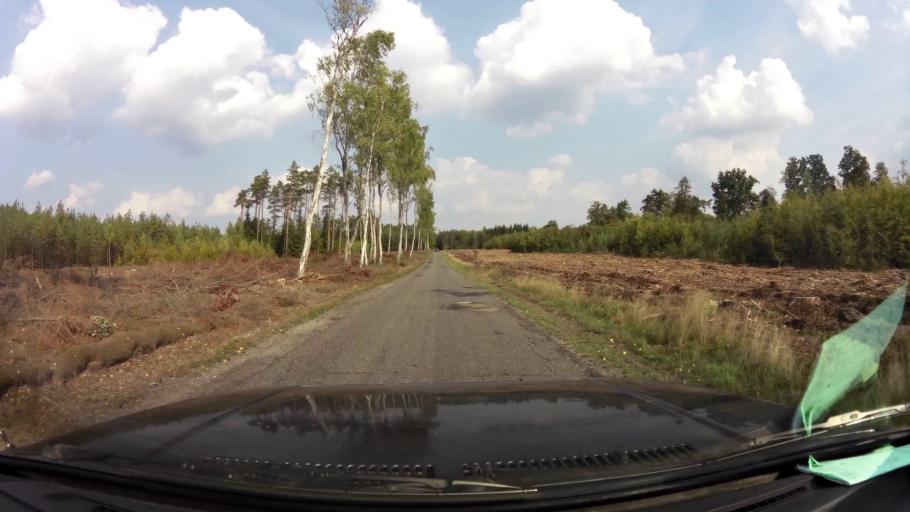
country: PL
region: West Pomeranian Voivodeship
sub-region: Powiat koszalinski
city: Bobolice
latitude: 54.0879
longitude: 16.4825
